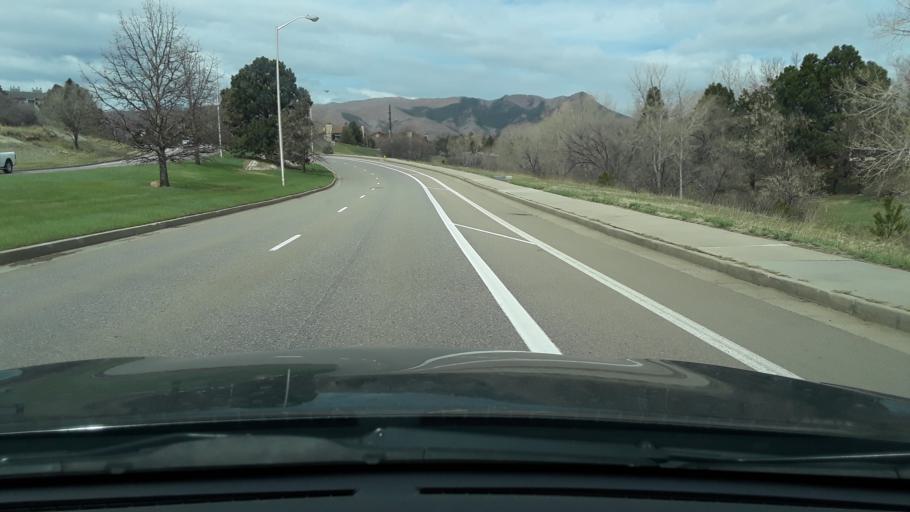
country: US
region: Colorado
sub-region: El Paso County
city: Air Force Academy
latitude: 38.9295
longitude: -104.8262
